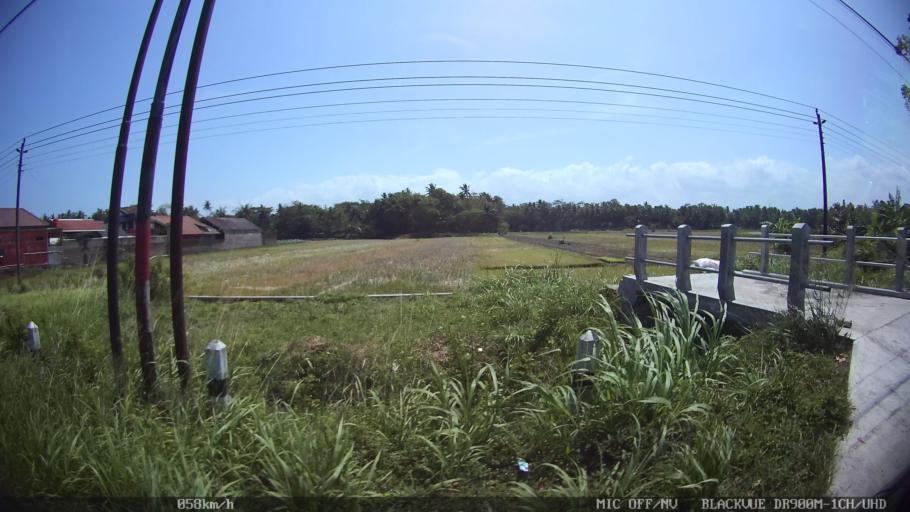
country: ID
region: Daerah Istimewa Yogyakarta
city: Srandakan
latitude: -7.9518
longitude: 110.2040
